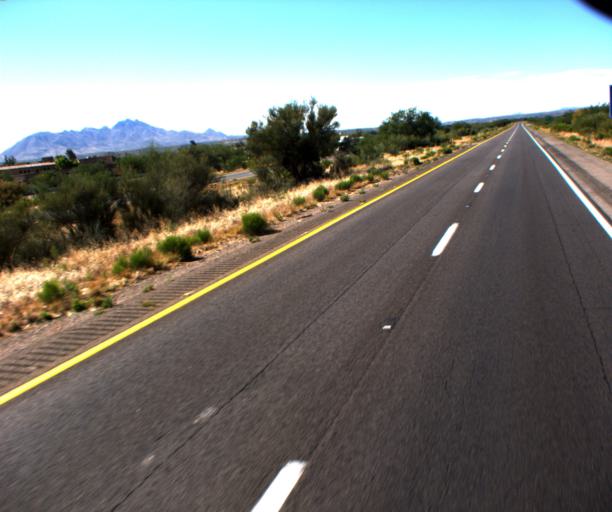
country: US
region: Arizona
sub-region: Santa Cruz County
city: Tubac
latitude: 31.6152
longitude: -111.0532
